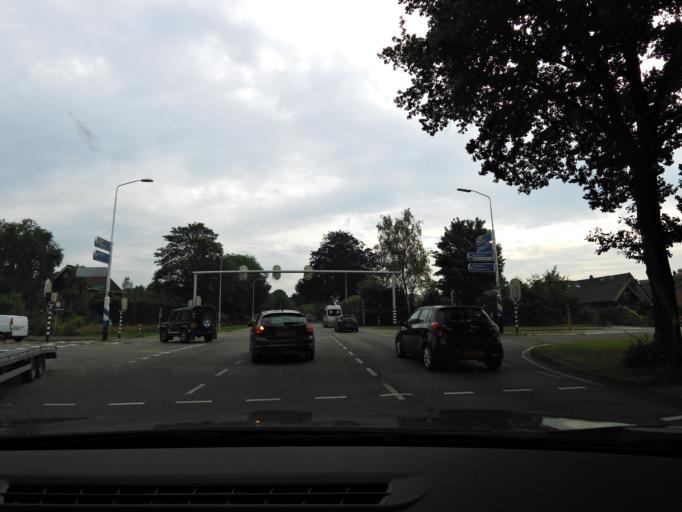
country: NL
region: Gelderland
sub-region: Gemeente Rheden
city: Spankeren
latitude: 52.0490
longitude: 6.1113
